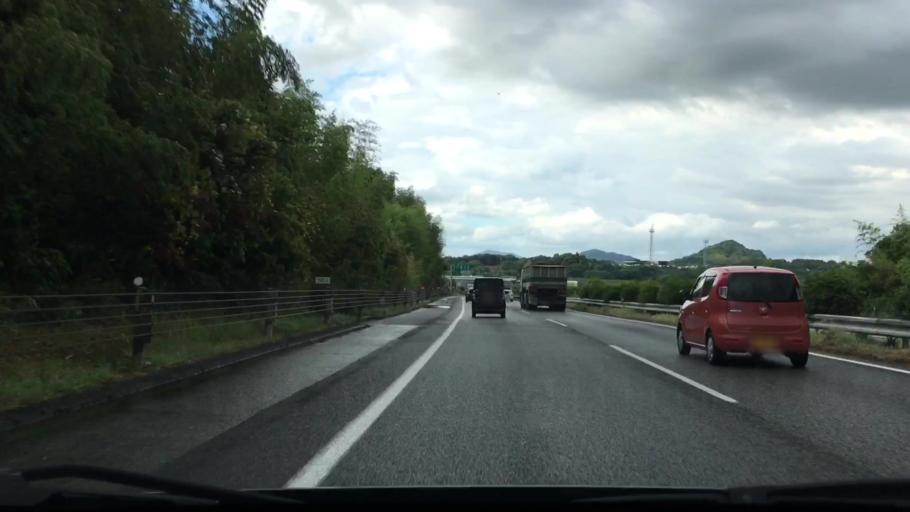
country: JP
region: Fukuoka
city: Koga
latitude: 33.7265
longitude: 130.5034
